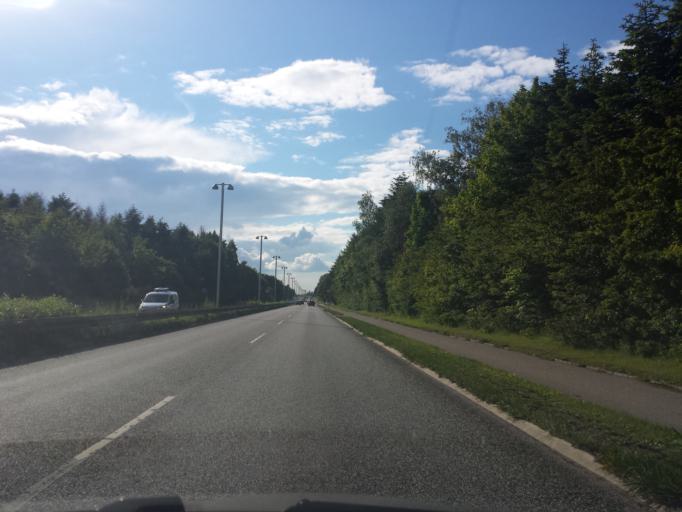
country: DK
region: Capital Region
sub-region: Ballerup Kommune
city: Ballerup
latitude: 55.7398
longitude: 12.3429
